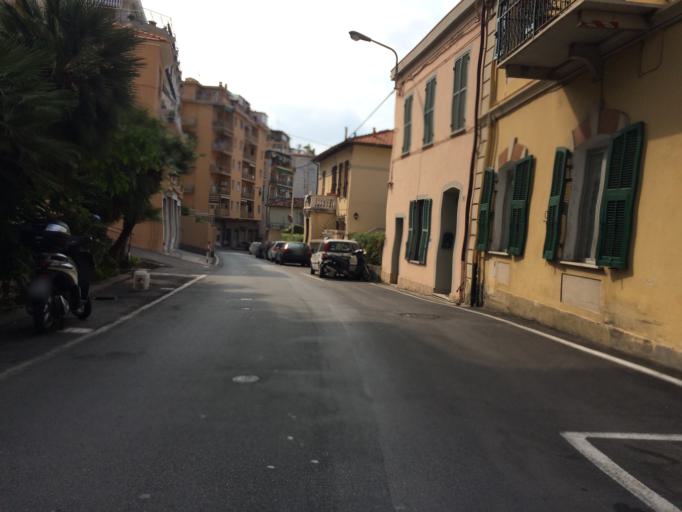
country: IT
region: Liguria
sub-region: Provincia di Imperia
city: San Remo
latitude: 43.8271
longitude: 7.7722
